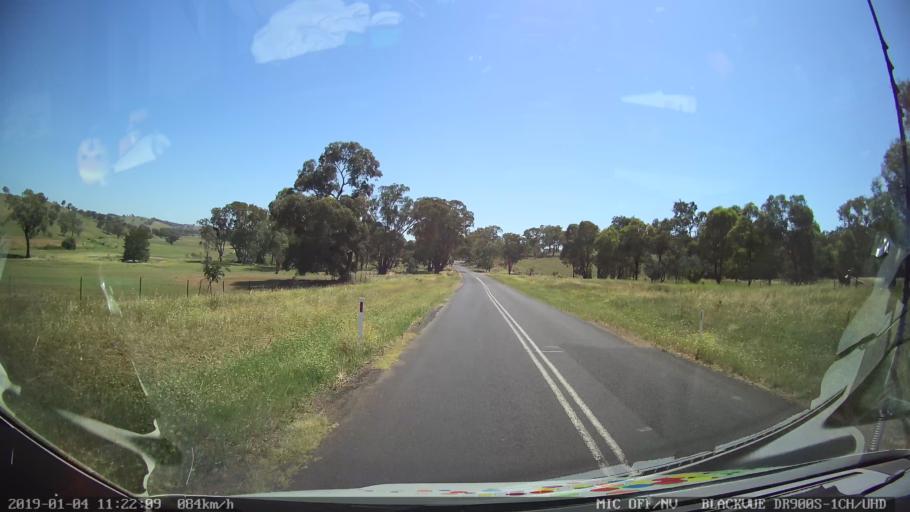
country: AU
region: New South Wales
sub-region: Cabonne
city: Molong
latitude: -33.1484
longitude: 148.7186
